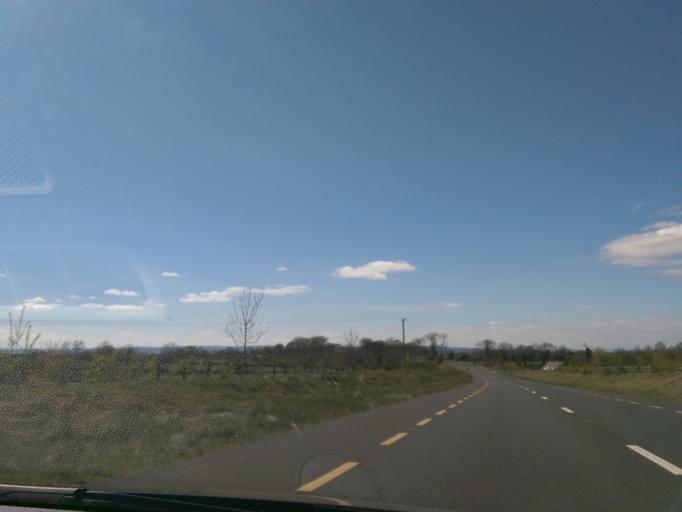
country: IE
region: Leinster
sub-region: Kildare
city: Moone
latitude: 52.9987
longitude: -6.8586
